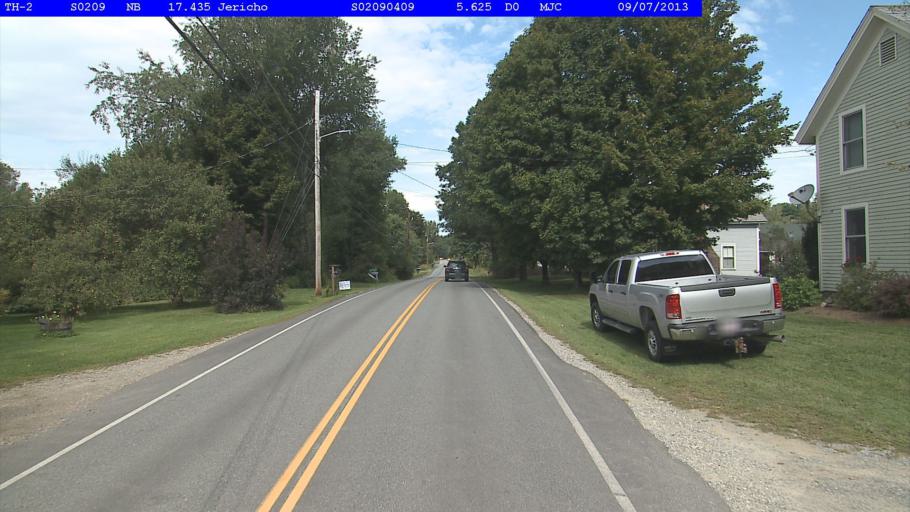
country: US
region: Vermont
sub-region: Chittenden County
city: Jericho
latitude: 44.5006
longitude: -72.9936
